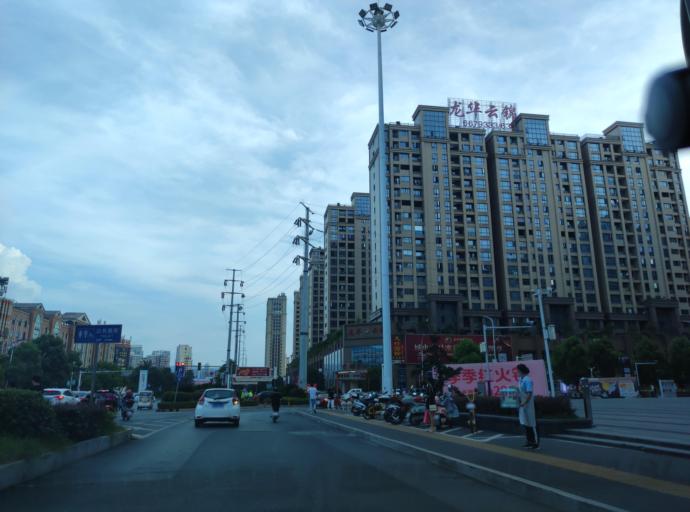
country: CN
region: Jiangxi Sheng
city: Pingxiang
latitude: 27.6339
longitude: 113.8691
